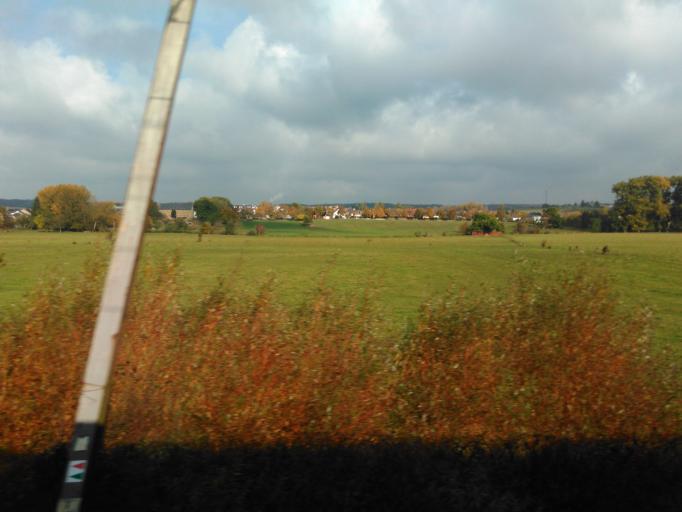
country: LU
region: Luxembourg
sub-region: Canton d'Esch-sur-Alzette
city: Bettembourg
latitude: 49.5149
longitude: 6.0814
